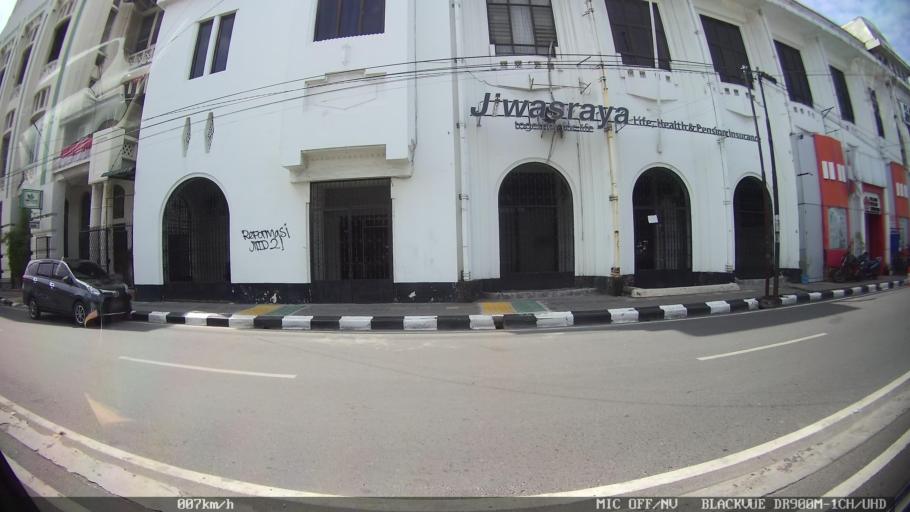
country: ID
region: North Sumatra
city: Medan
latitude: 3.5845
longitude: 98.6803
